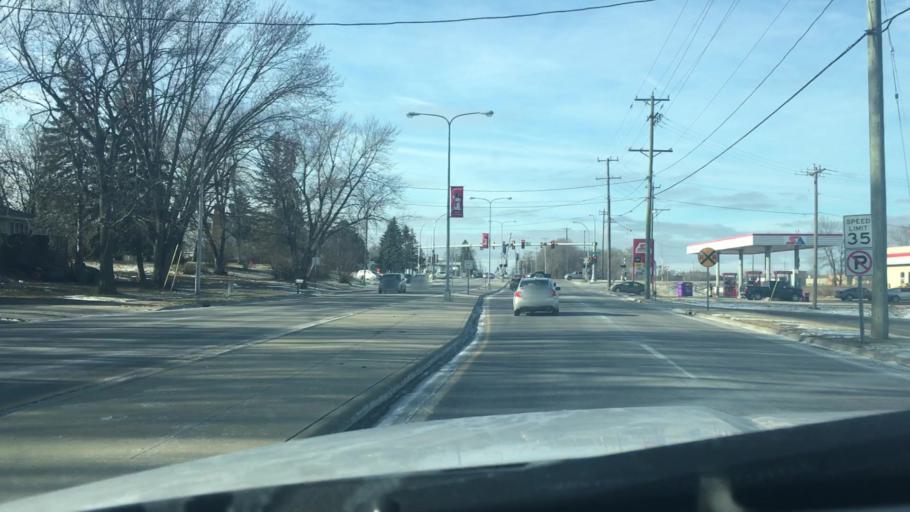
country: US
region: Minnesota
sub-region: Stearns County
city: Waite Park
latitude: 45.5589
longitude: -94.2115
